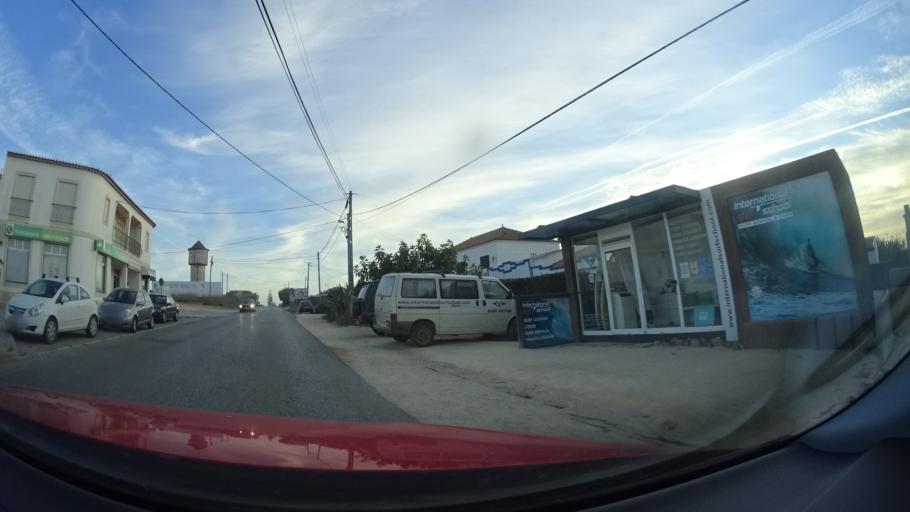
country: PT
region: Faro
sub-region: Vila do Bispo
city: Sagres
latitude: 37.0103
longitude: -8.9436
